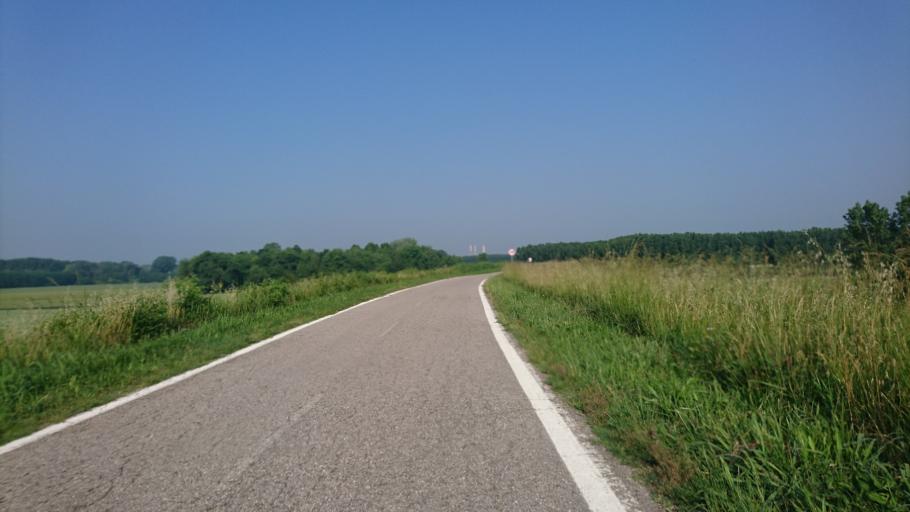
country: IT
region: Veneto
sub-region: Provincia di Rovigo
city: Castelnovo Bariano
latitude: 45.0214
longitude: 11.2905
